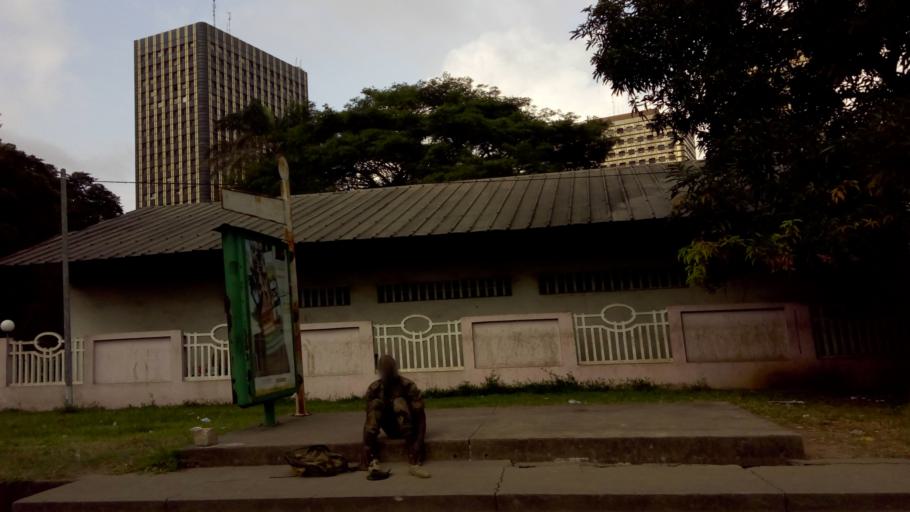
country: CI
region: Lagunes
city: Abidjan
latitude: 5.3336
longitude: -4.0245
